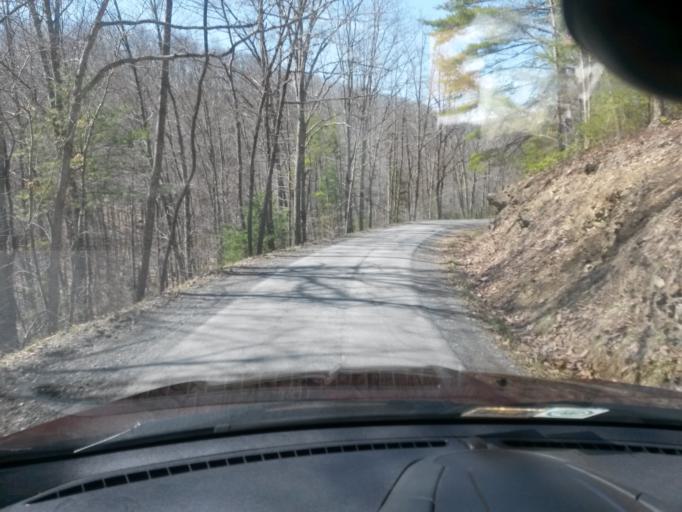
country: US
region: West Virginia
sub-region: Greenbrier County
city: White Sulphur Springs
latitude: 37.6786
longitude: -80.3317
